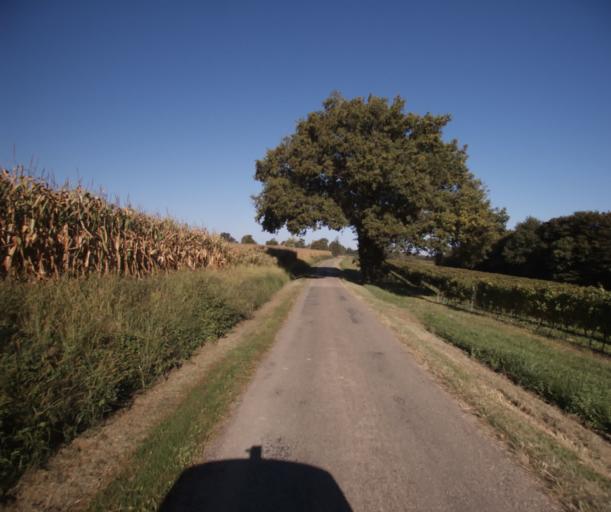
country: FR
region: Midi-Pyrenees
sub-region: Departement du Gers
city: Cazaubon
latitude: 43.9099
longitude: 0.0059
